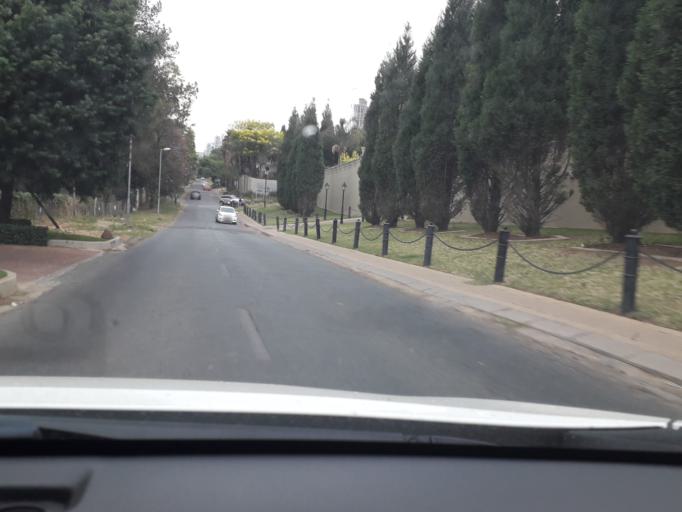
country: ZA
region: Gauteng
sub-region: City of Johannesburg Metropolitan Municipality
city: Johannesburg
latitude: -26.1162
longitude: 28.0431
